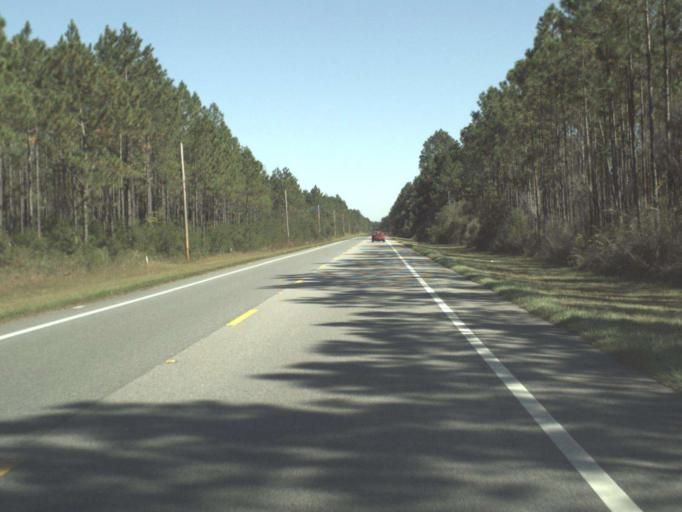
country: US
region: Florida
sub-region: Bay County
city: Lynn Haven
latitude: 30.3273
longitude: -85.7101
